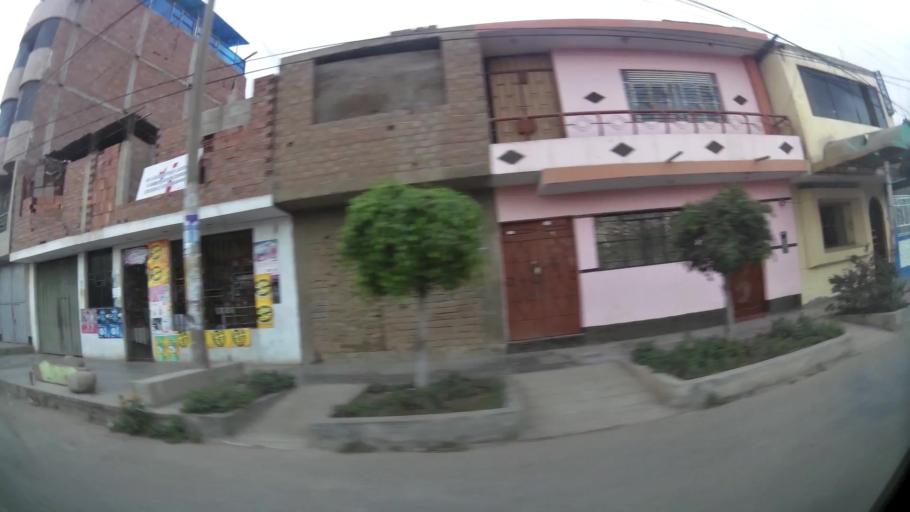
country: PE
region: La Libertad
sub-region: Provincia de Trujillo
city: El Porvenir
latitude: -8.0814
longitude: -79.0187
